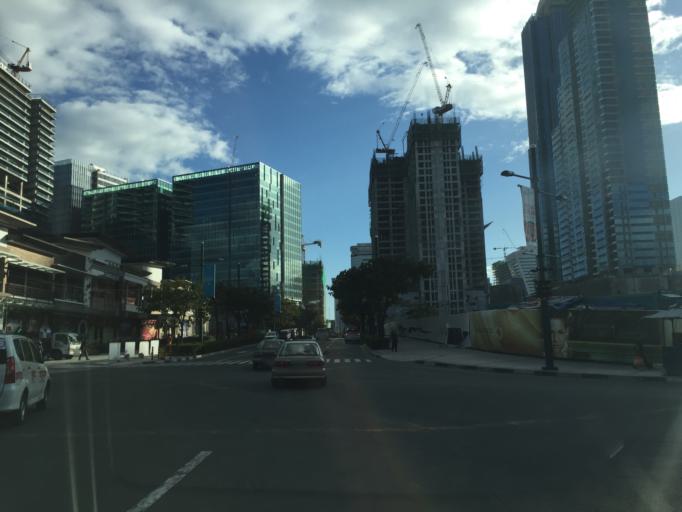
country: PH
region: Metro Manila
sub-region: Makati City
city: Makati City
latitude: 14.5593
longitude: 121.0542
